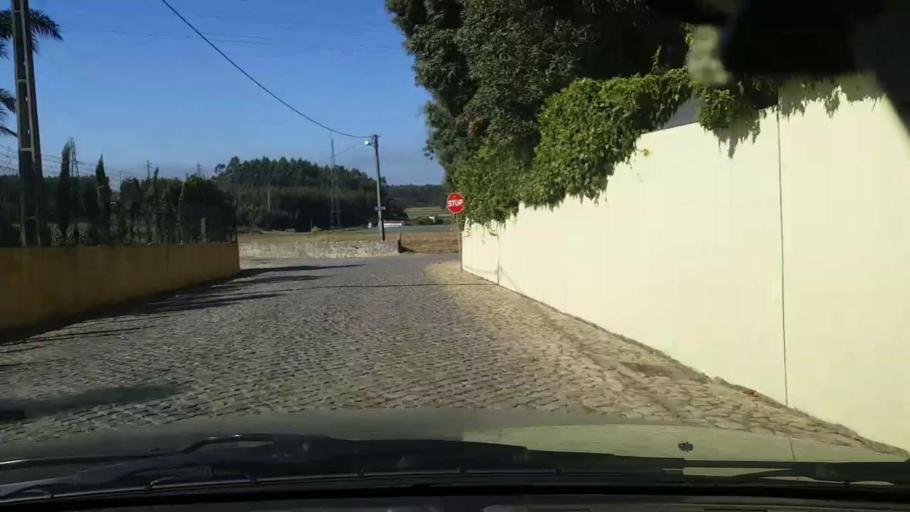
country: PT
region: Porto
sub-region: Maia
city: Gemunde
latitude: 41.2879
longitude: -8.6469
